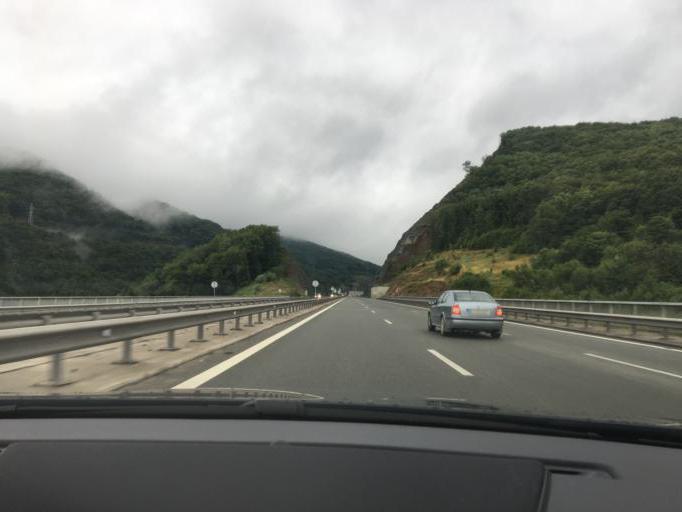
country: BG
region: Sofiya
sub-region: Obshtina Bozhurishte
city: Bozhurishte
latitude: 42.6772
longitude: 23.1520
